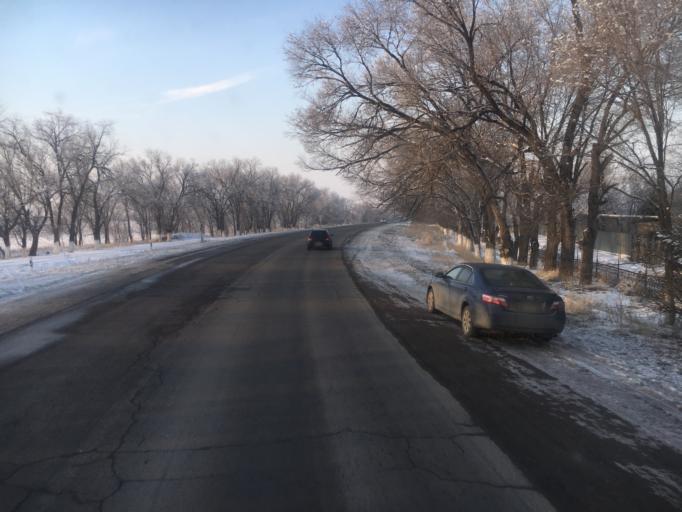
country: KZ
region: Almaty Oblysy
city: Burunday
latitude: 43.3081
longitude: 76.6669
